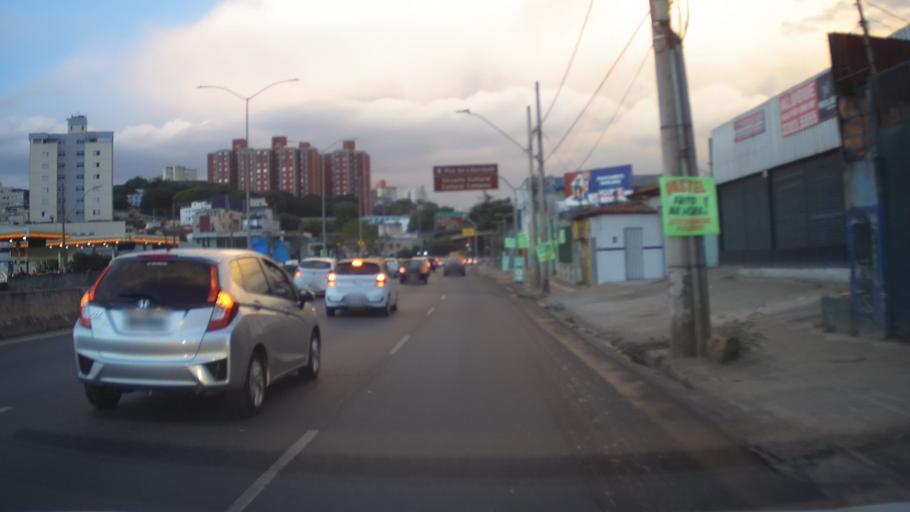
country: BR
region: Minas Gerais
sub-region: Belo Horizonte
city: Belo Horizonte
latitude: -19.9207
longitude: -43.9696
